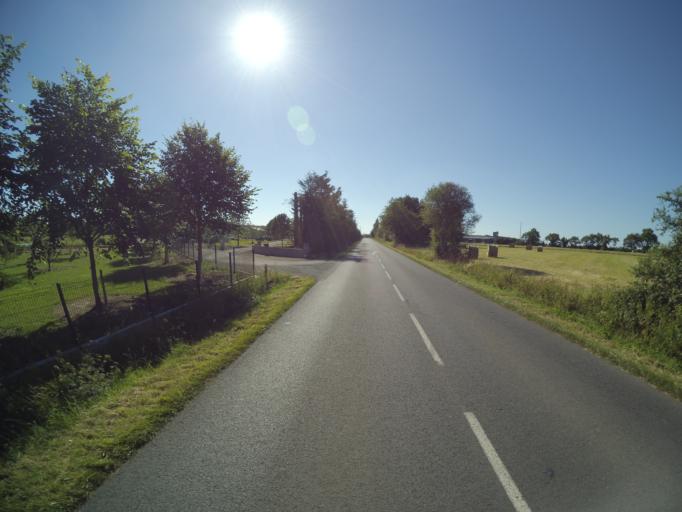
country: FR
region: Pays de la Loire
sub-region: Departement de la Vendee
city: La Guyonniere
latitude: 46.9544
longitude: -1.2223
